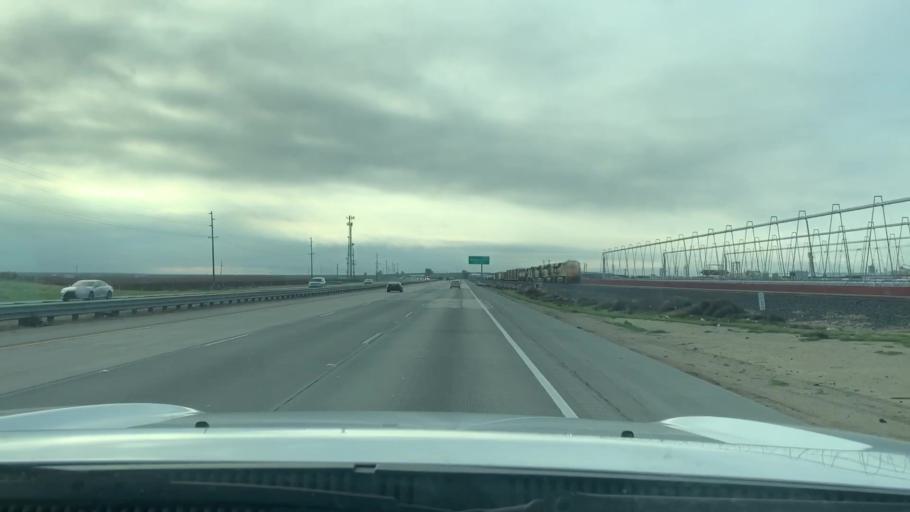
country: US
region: California
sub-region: Kern County
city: Shafter
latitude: 35.5701
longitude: -119.2011
